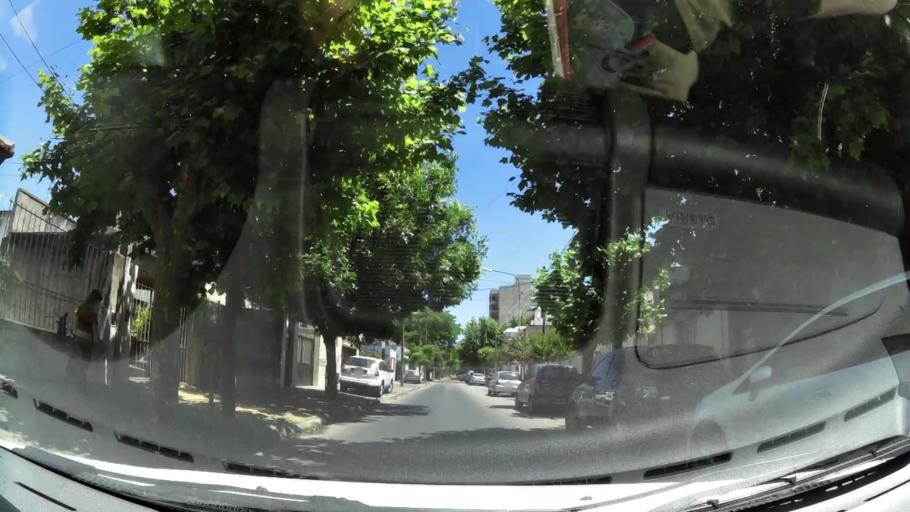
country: AR
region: Buenos Aires
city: Caseros
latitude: -34.5983
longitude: -58.5385
